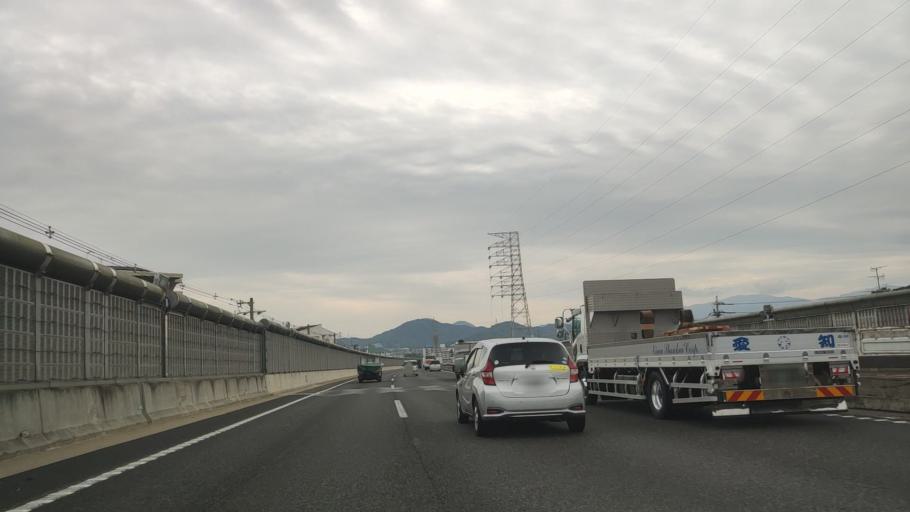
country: JP
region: Osaka
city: Kashihara
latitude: 34.5669
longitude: 135.6104
